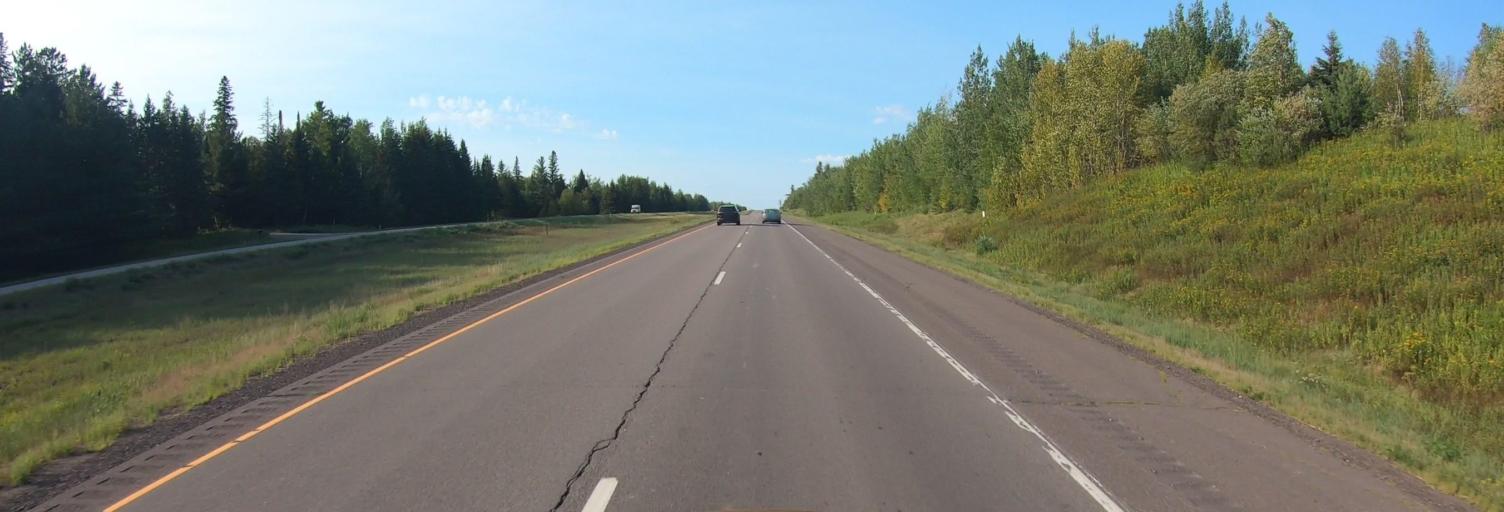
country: US
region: Minnesota
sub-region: Carlton County
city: Cloquet
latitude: 47.0022
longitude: -92.4709
